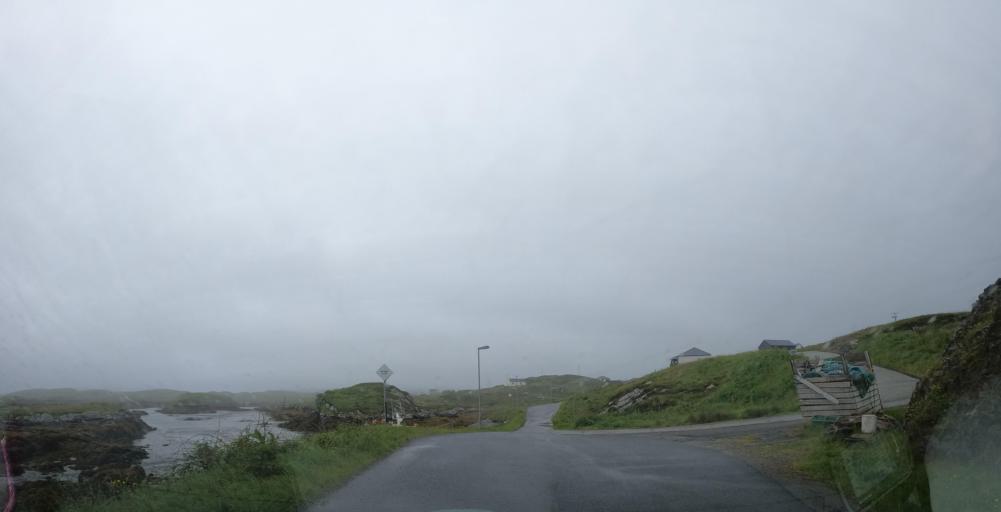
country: GB
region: Scotland
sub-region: Eilean Siar
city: Barra
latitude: 56.9991
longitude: -7.4204
